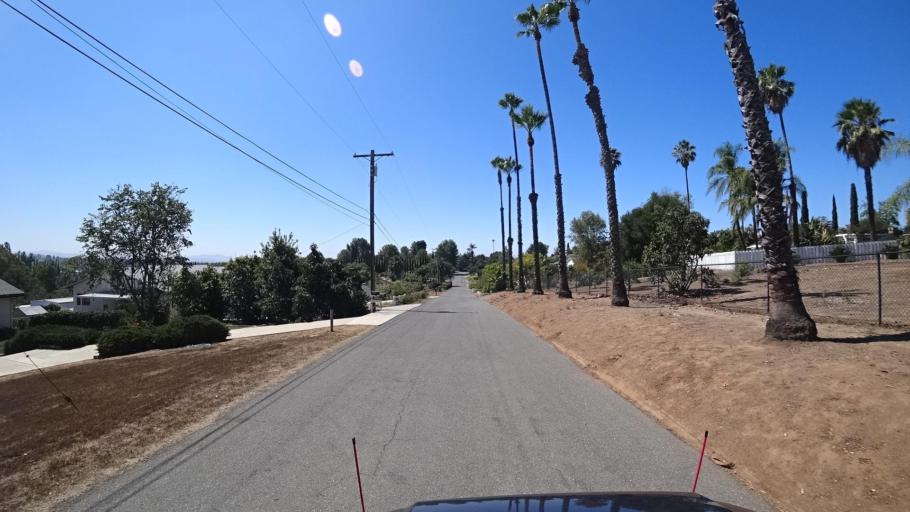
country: US
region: California
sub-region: San Diego County
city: Fallbrook
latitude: 33.3616
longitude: -117.2186
